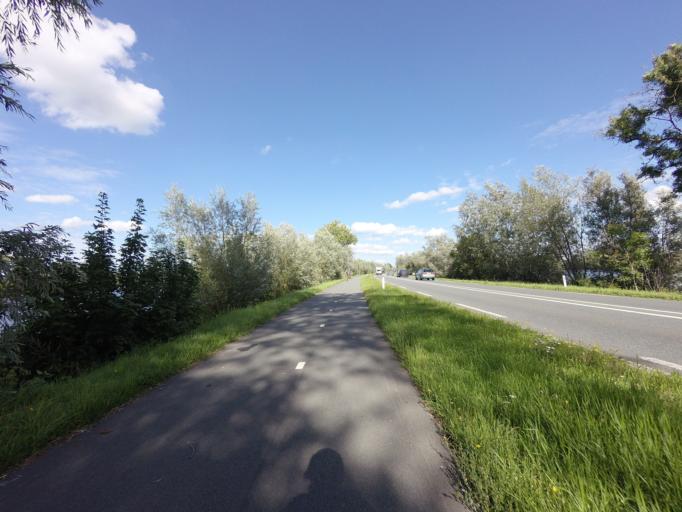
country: NL
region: Utrecht
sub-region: Stichtse Vecht
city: Breukelen
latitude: 52.2190
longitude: 4.9390
